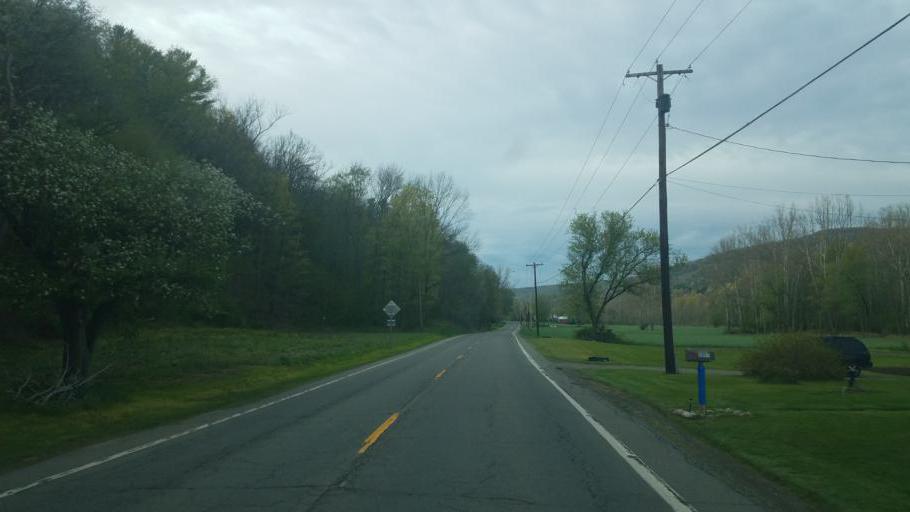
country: US
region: New York
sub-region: Steuben County
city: Canisteo
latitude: 42.2356
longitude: -77.5787
